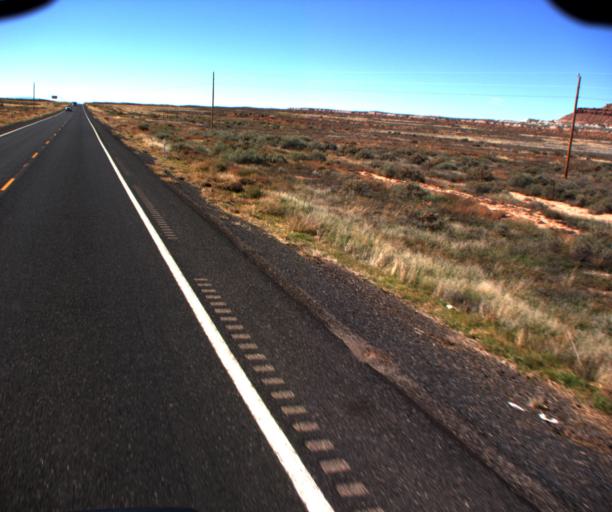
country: US
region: Arizona
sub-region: Coconino County
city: Fredonia
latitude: 36.9247
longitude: -112.5684
